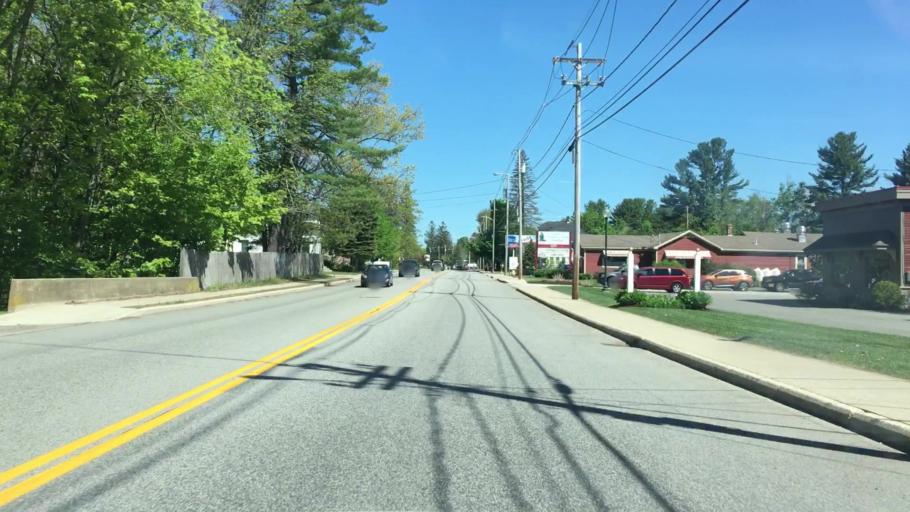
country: US
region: Maine
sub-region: York County
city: Springvale
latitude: 43.4547
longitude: -70.7896
